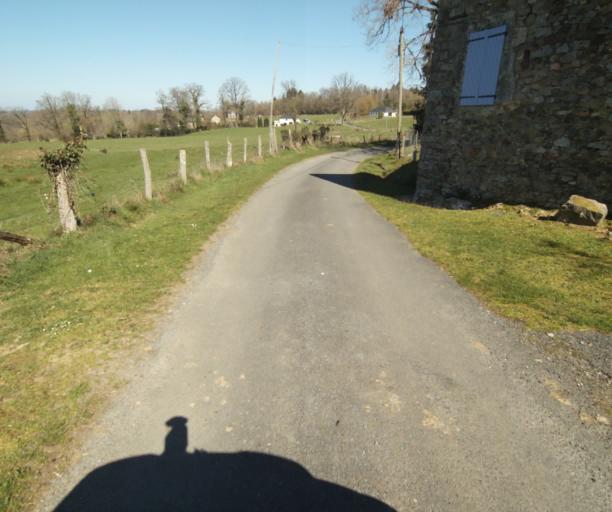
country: FR
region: Limousin
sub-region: Departement de la Correze
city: Saint-Mexant
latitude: 45.3227
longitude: 1.6491
